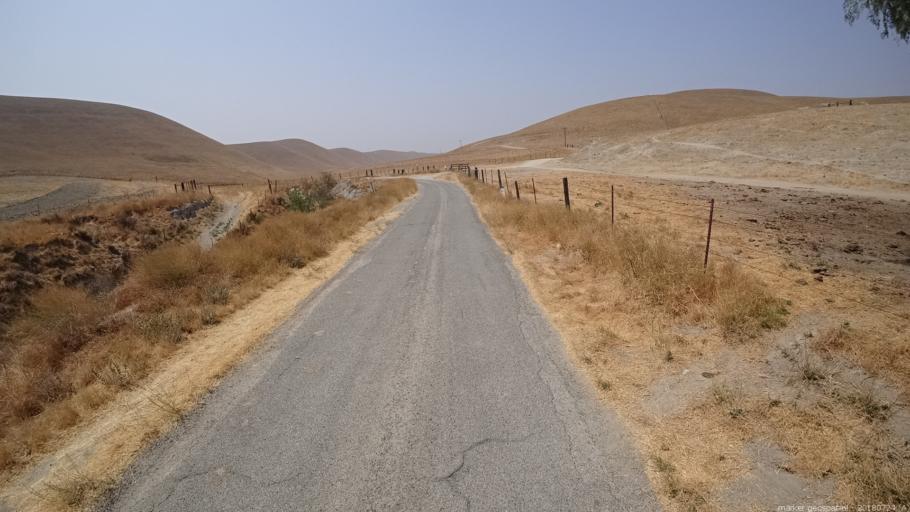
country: US
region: California
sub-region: Monterey County
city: King City
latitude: 36.1918
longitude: -120.9648
